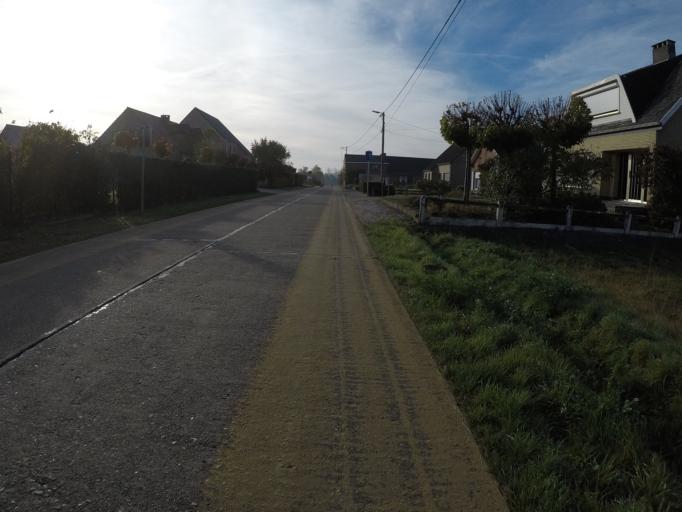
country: BE
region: Flanders
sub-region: Provincie Vlaams-Brabant
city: Begijnendijk
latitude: 50.9885
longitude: 4.7750
